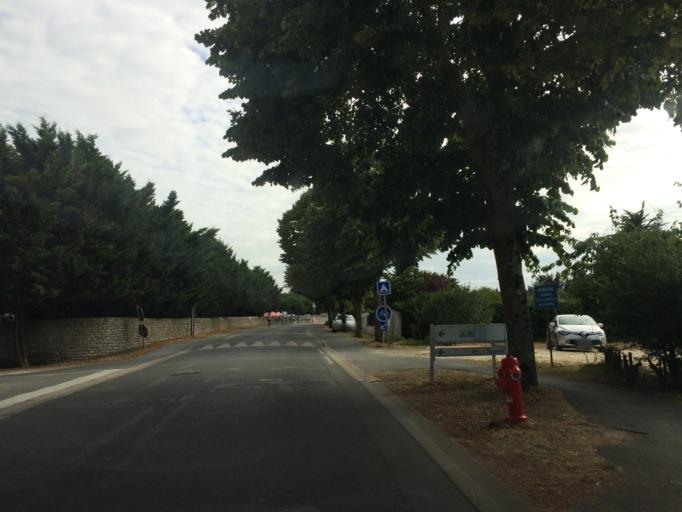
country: FR
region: Poitou-Charentes
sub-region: Departement de la Charente-Maritime
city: La Flotte
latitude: 46.1823
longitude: -1.3313
